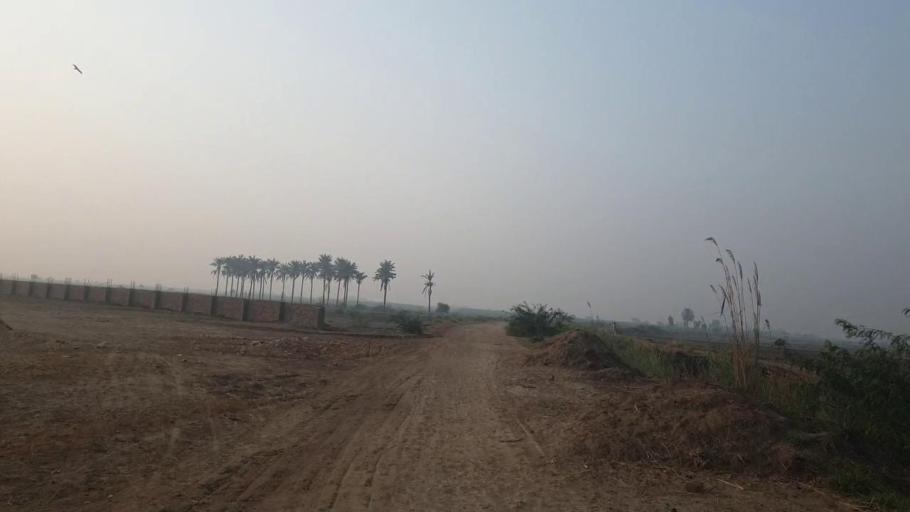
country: PK
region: Sindh
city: Tando Jam
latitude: 25.3285
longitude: 68.4774
